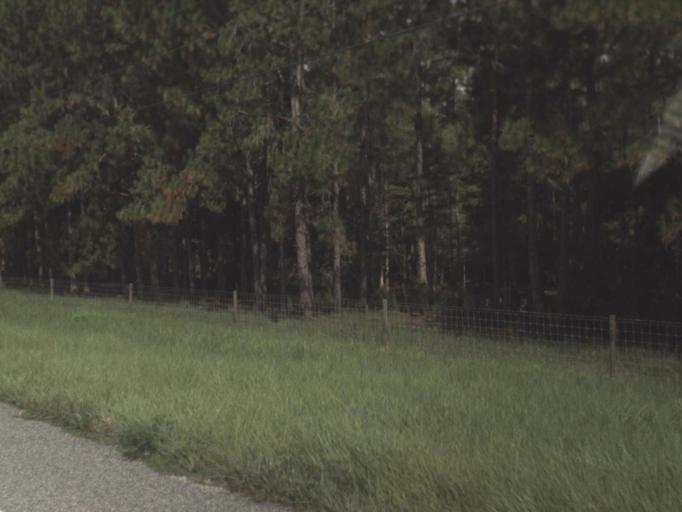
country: US
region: Florida
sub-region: Pasco County
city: Land O' Lakes
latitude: 28.3222
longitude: -82.4308
